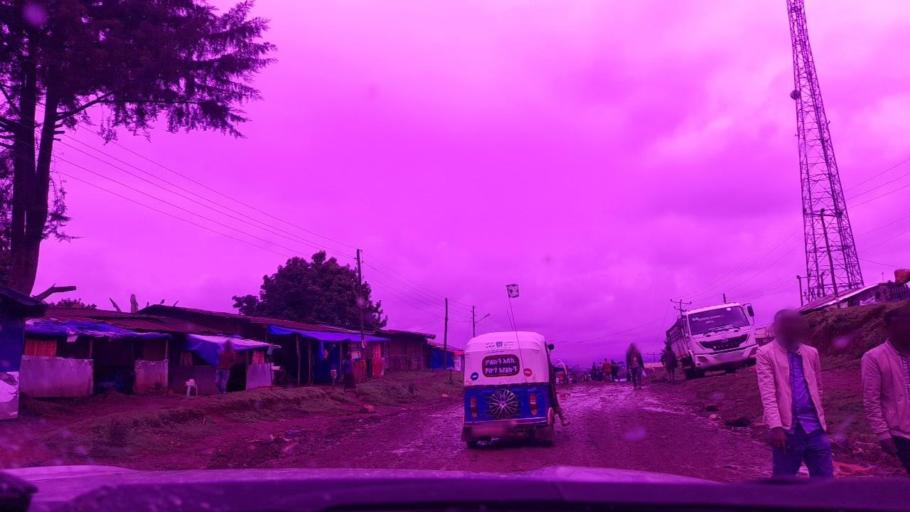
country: ET
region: Southern Nations, Nationalities, and People's Region
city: Tippi
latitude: 7.5943
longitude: 35.7606
